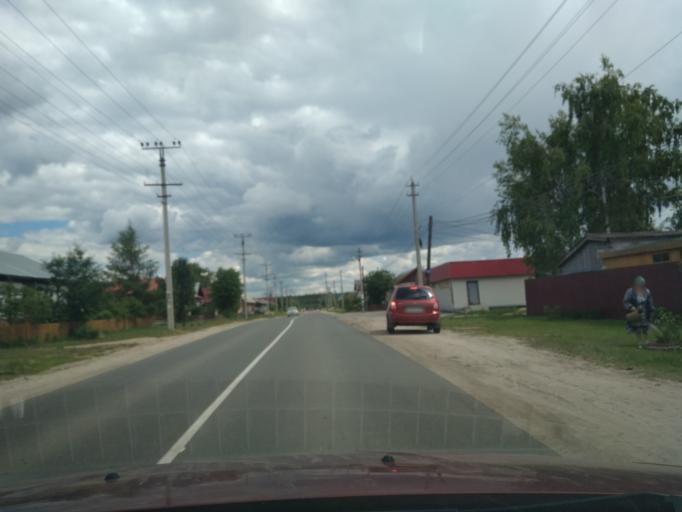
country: RU
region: Vladimir
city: Melenki
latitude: 55.3384
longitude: 41.6484
